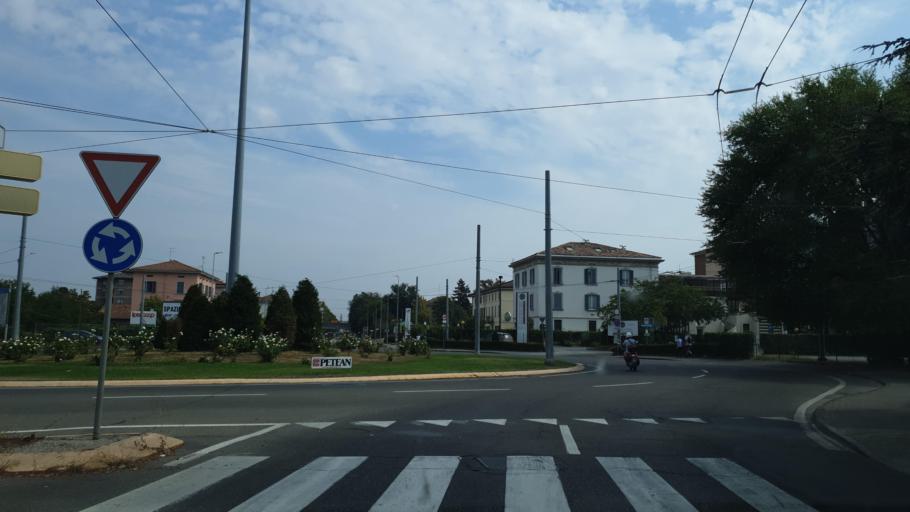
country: IT
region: Emilia-Romagna
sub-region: Provincia di Parma
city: Parma
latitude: 44.8073
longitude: 10.2993
